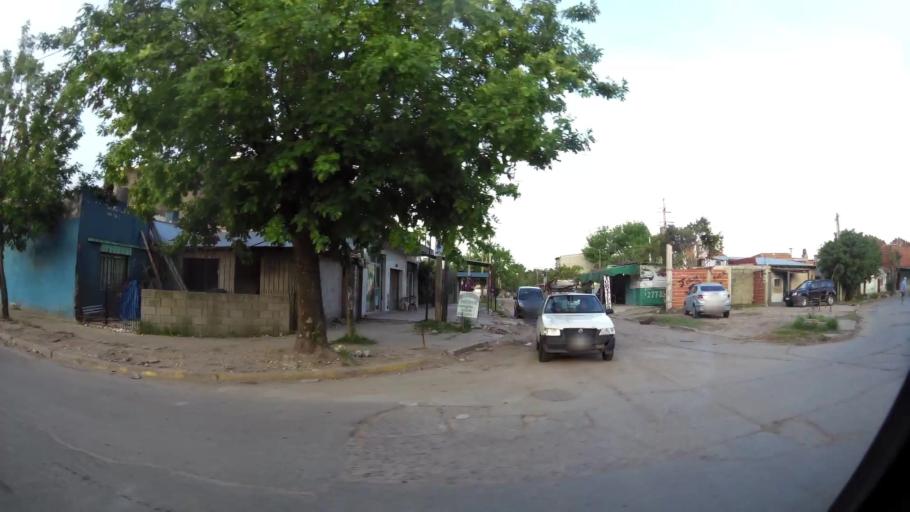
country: AR
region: Buenos Aires
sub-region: Partido de Almirante Brown
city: Adrogue
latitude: -34.7786
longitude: -58.3206
